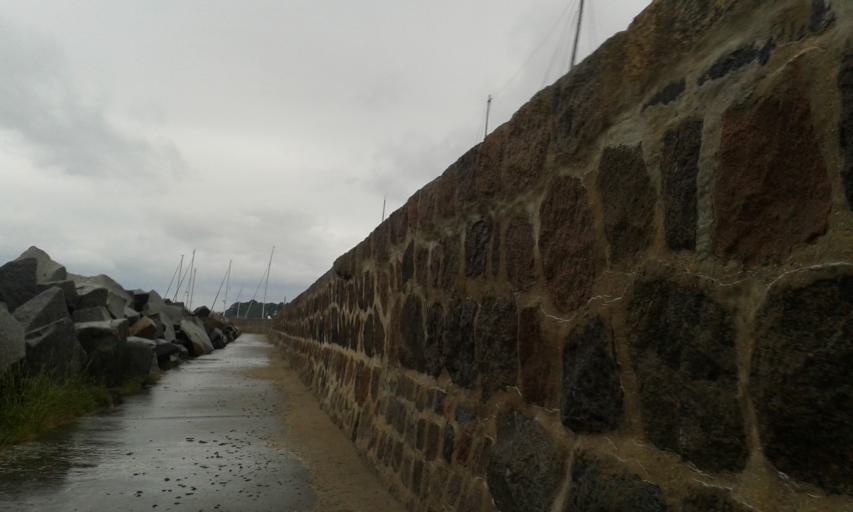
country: DE
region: Mecklenburg-Vorpommern
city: Sassnitz
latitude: 54.5131
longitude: 13.6490
